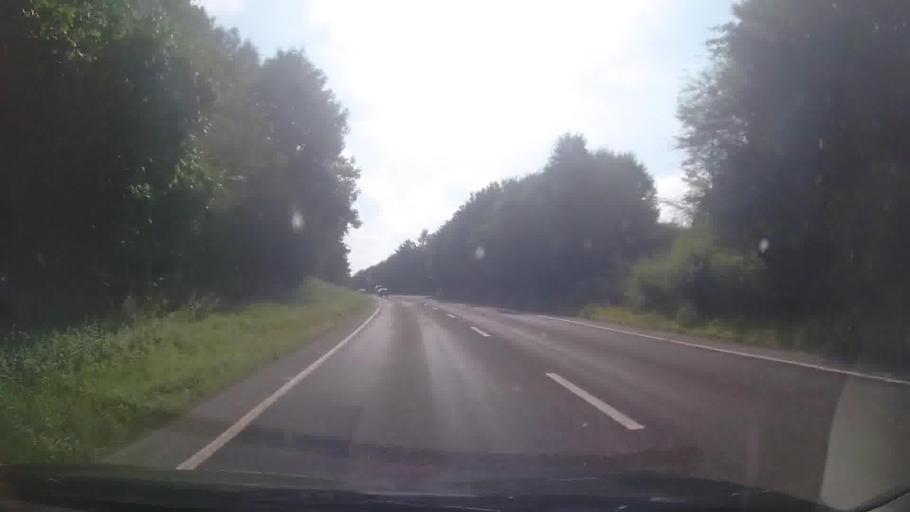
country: GB
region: England
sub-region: Shropshire
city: Whitchurch
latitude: 52.9733
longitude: -2.7084
